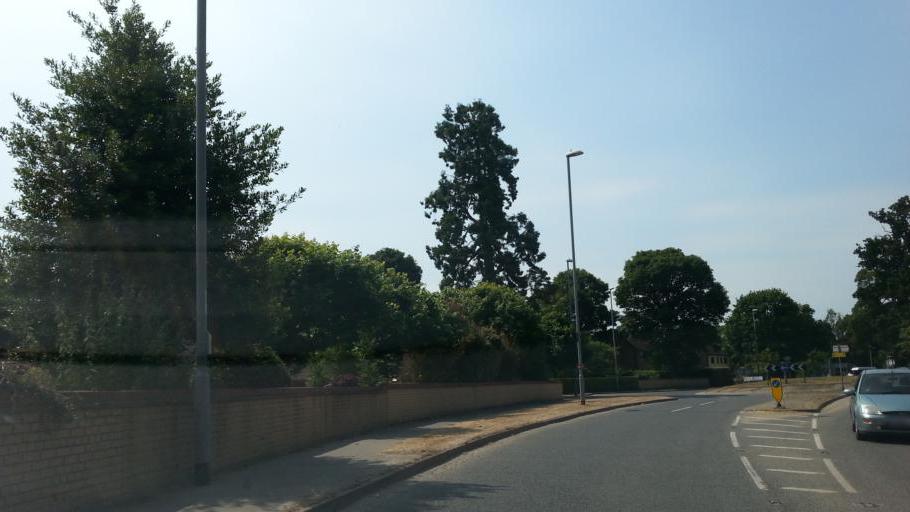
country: GB
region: England
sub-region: Cambridgeshire
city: Brampton
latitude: 52.3177
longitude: -0.2206
